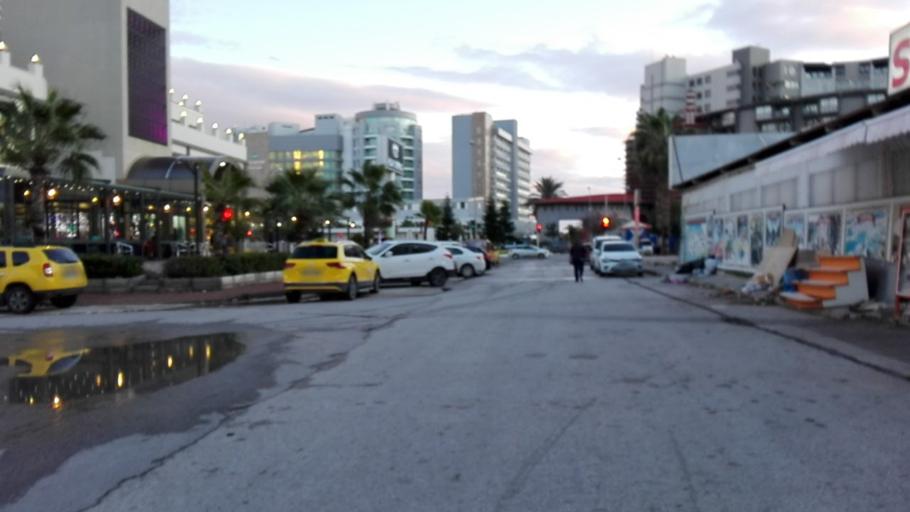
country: TR
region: Antalya
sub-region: Serik
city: Kumkoey
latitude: 36.8578
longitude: 30.8809
